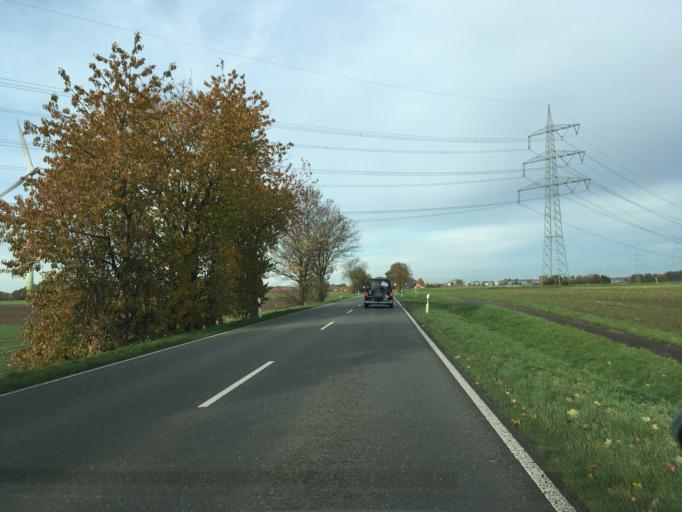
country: DE
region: North Rhine-Westphalia
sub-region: Regierungsbezirk Munster
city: Heiden
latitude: 51.8049
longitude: 6.9515
